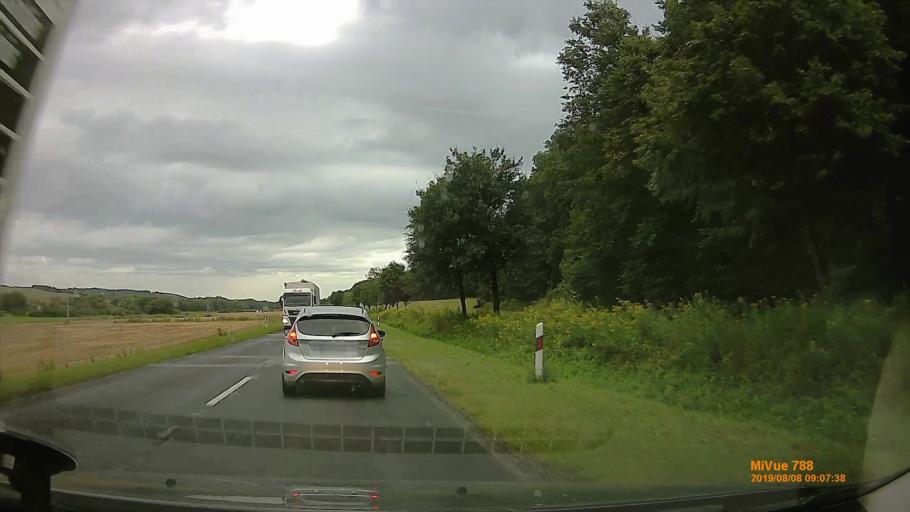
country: HU
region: Zala
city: Zalaegerszeg
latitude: 46.7364
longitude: 16.8560
